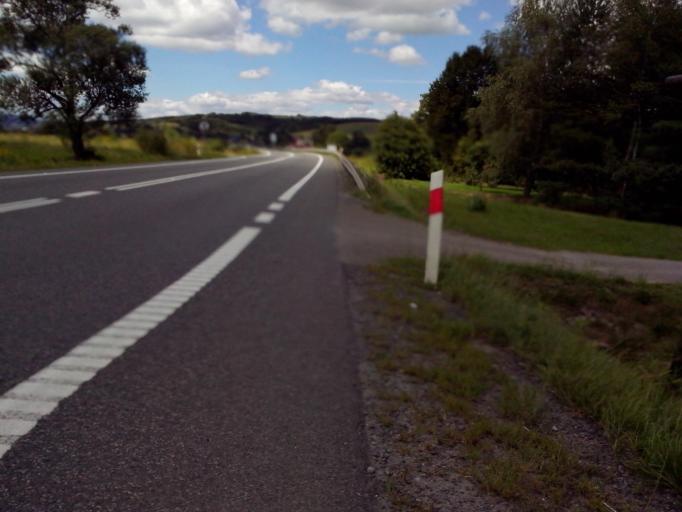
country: PL
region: Subcarpathian Voivodeship
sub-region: Powiat brzozowski
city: Domaradz
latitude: 49.7981
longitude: 21.9347
